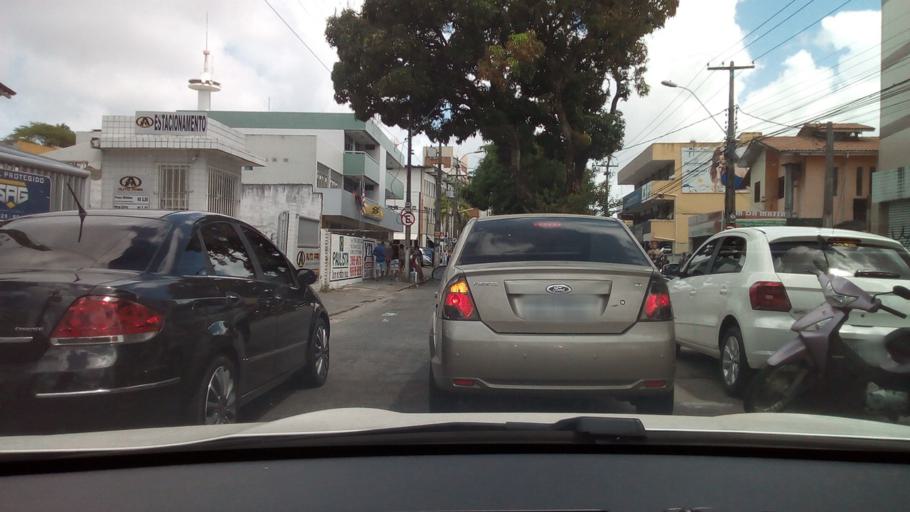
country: BR
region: Paraiba
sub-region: Joao Pessoa
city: Joao Pessoa
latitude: -7.1166
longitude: -34.8795
